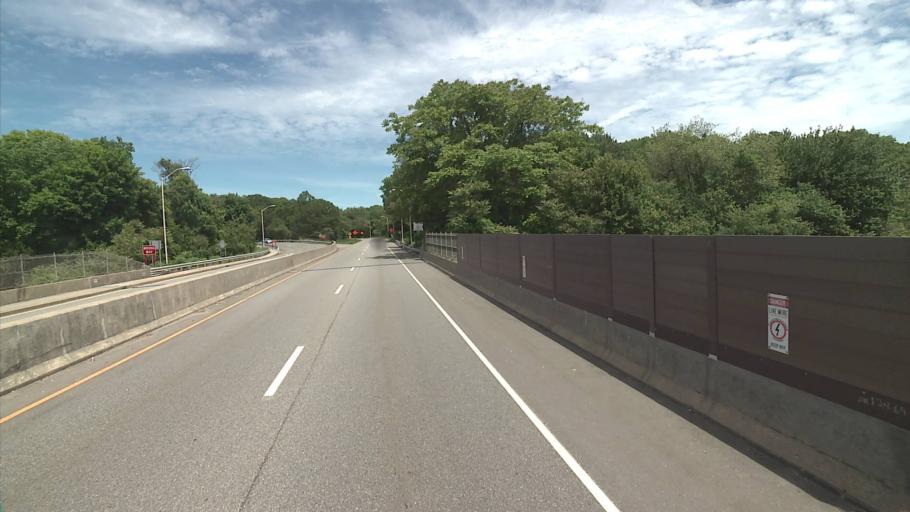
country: US
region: Connecticut
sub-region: New London County
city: Groton
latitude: 41.3620
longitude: -72.0771
